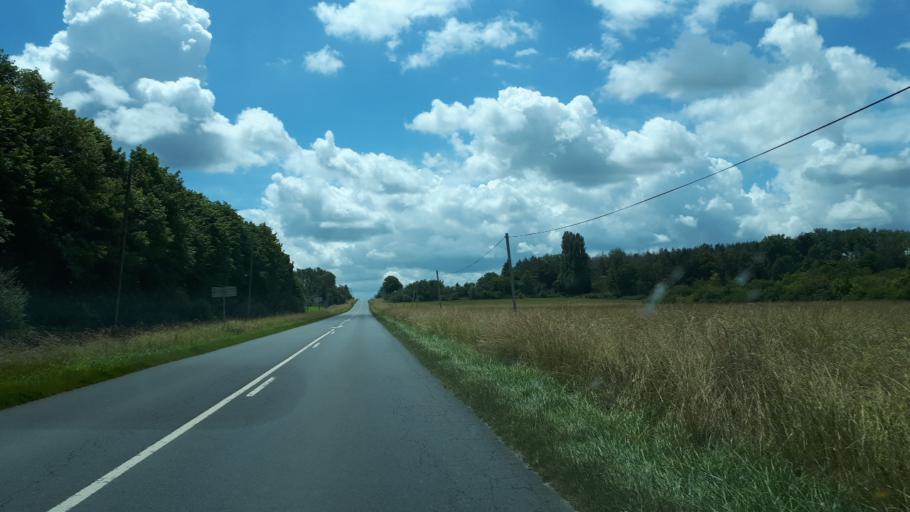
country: FR
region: Centre
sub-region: Departement du Loir-et-Cher
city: Contres
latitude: 47.4084
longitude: 1.4211
